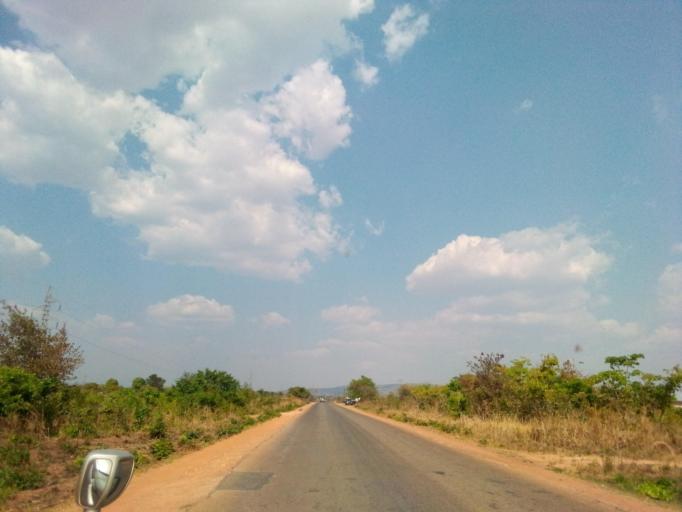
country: ZM
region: Northern
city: Mpika
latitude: -11.8329
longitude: 31.4077
